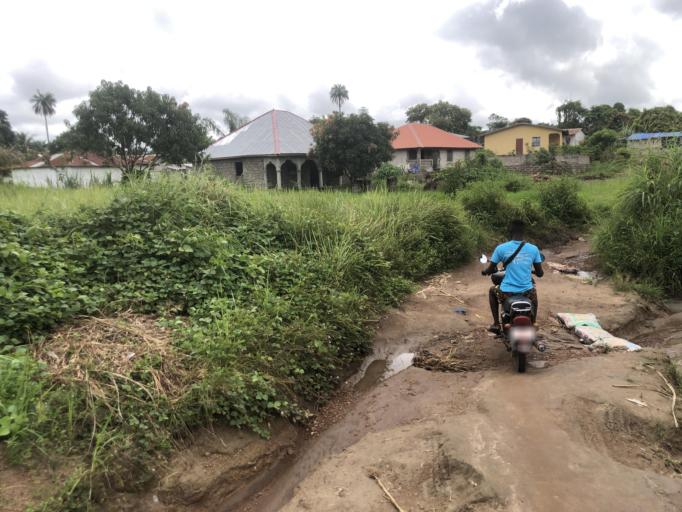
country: SL
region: Northern Province
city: Makeni
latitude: 8.9110
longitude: -12.0429
